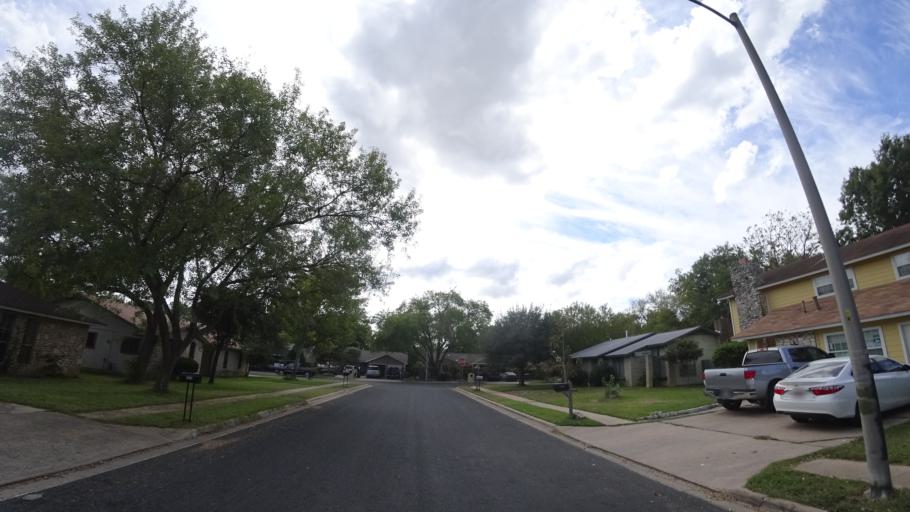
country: US
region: Texas
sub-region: Travis County
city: Austin
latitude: 30.1988
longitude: -97.7409
